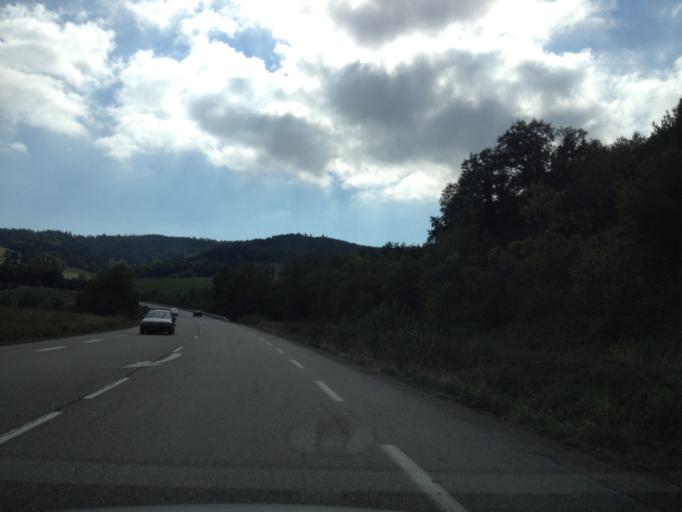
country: FR
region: Rhone-Alpes
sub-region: Departement de la Loire
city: Lentigny
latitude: 45.9310
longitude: 3.9750
